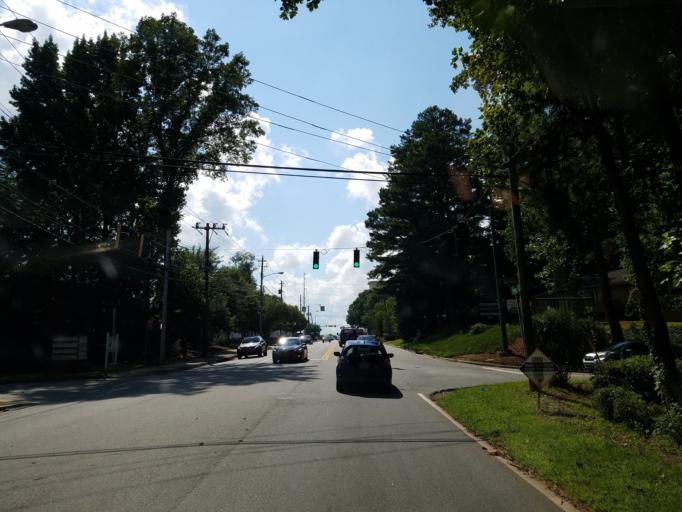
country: US
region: Georgia
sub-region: Fulton County
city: Sandy Springs
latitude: 33.9191
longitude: -84.3764
